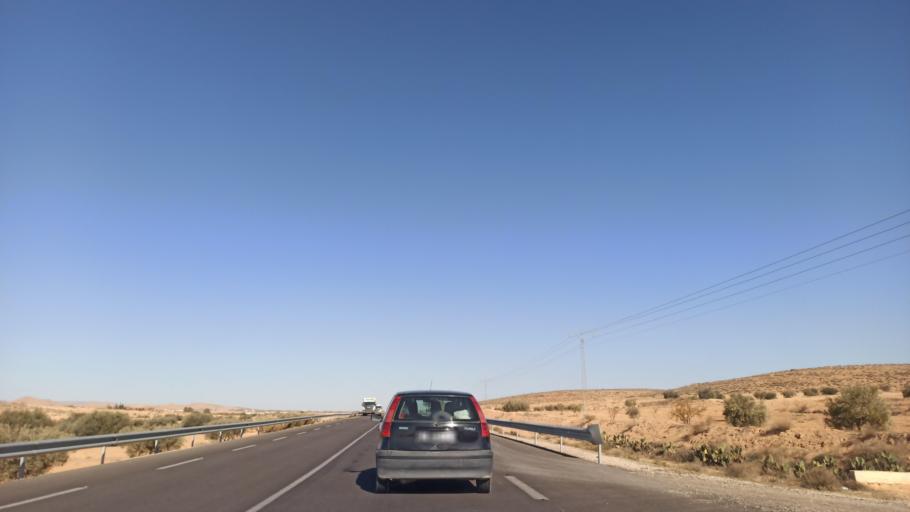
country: TN
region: Sidi Bu Zayd
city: Bi'r al Hufayy
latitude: 34.7197
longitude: 9.0599
